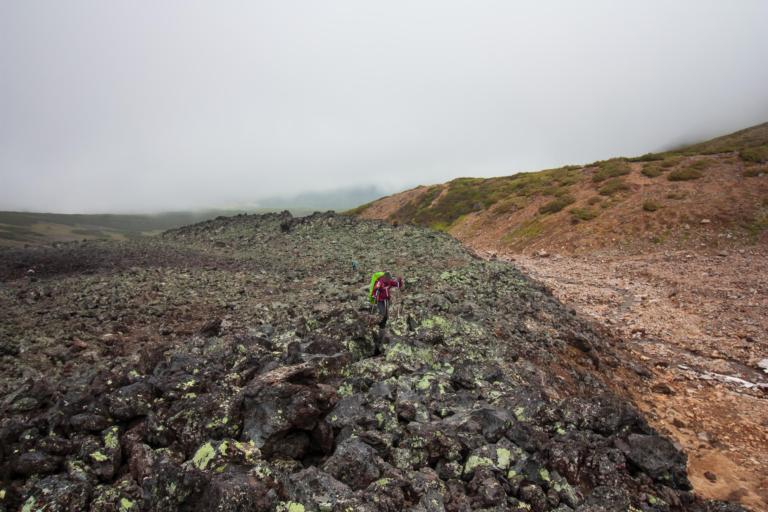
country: RU
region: Kamtsjatka
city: Petropavlovsk-Kamchatsky
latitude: 53.6162
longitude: 158.9411
